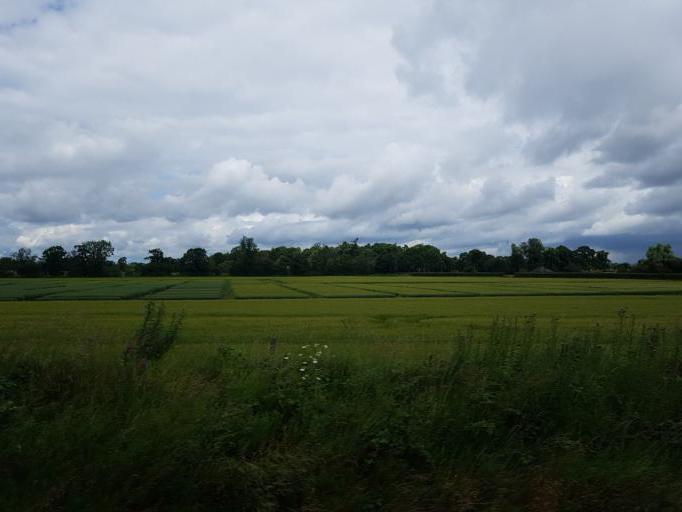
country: GB
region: Scotland
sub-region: Edinburgh
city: Currie
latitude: 55.9259
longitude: -3.3263
